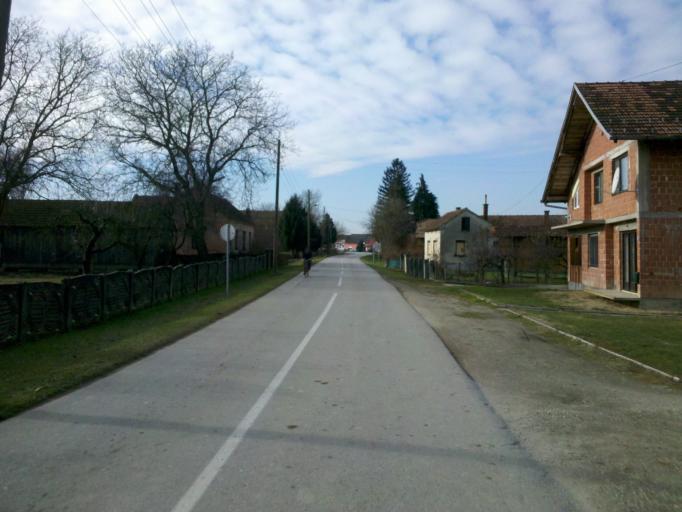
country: HR
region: Koprivnicko-Krizevacka
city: Kalinovac
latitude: 46.1003
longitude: 17.1392
